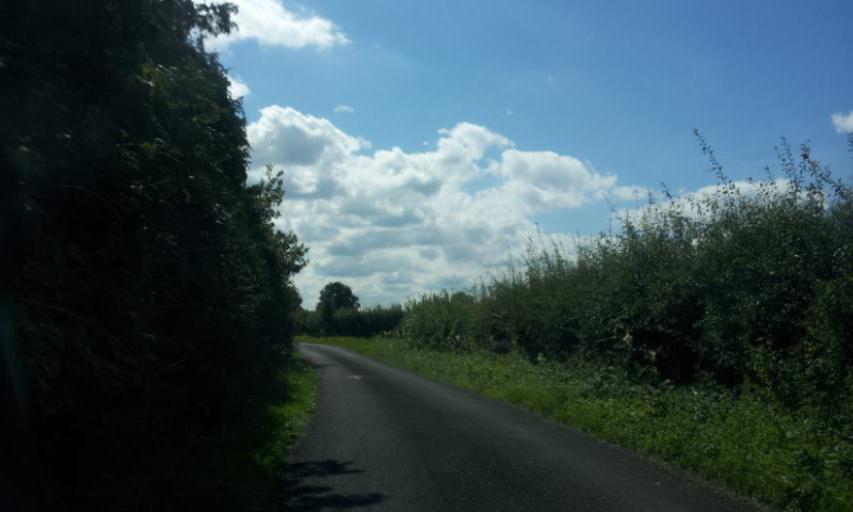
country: GB
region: England
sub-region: Kent
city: Marden
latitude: 51.1927
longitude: 0.4938
